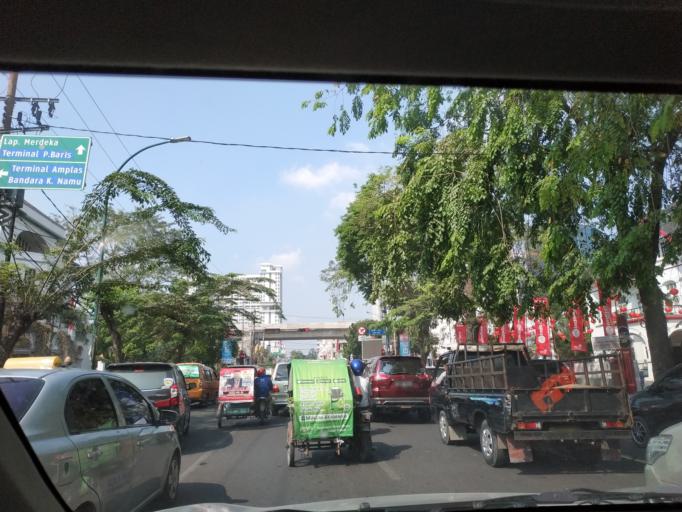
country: ID
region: North Sumatra
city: Medan
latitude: 3.5941
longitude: 98.6800
